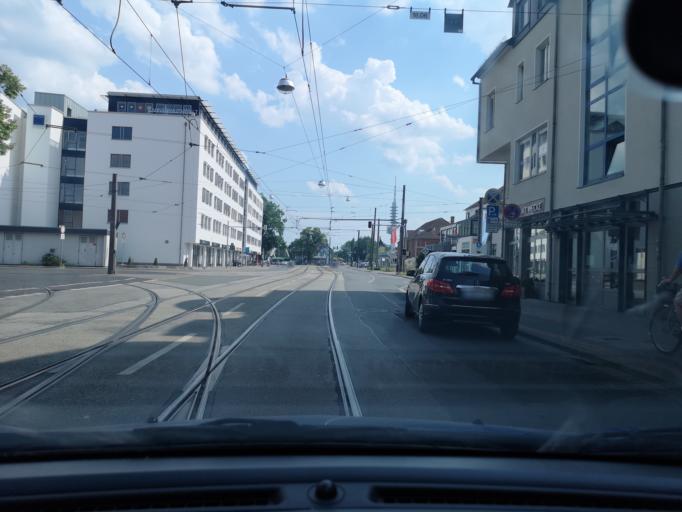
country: DE
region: Lower Saxony
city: Langenhagen
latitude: 52.4079
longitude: 9.7998
